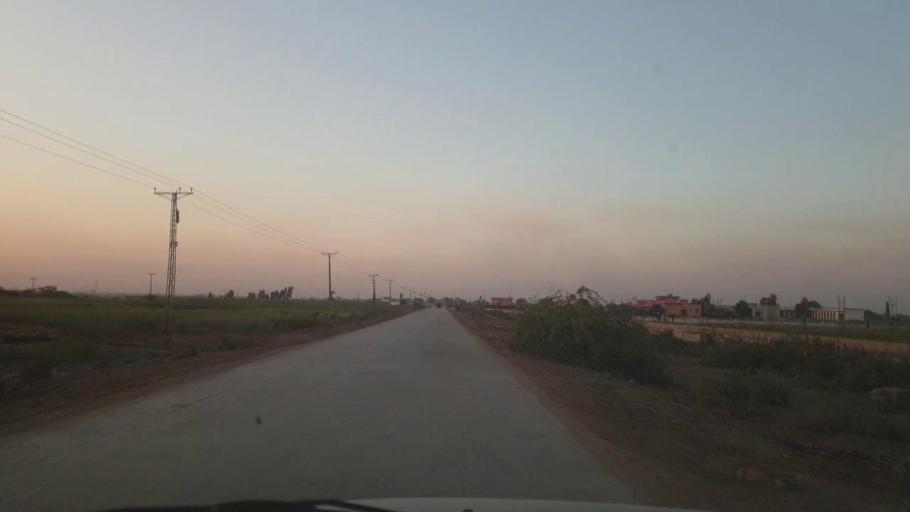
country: PK
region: Sindh
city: Mirpur Khas
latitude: 25.4923
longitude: 69.0392
